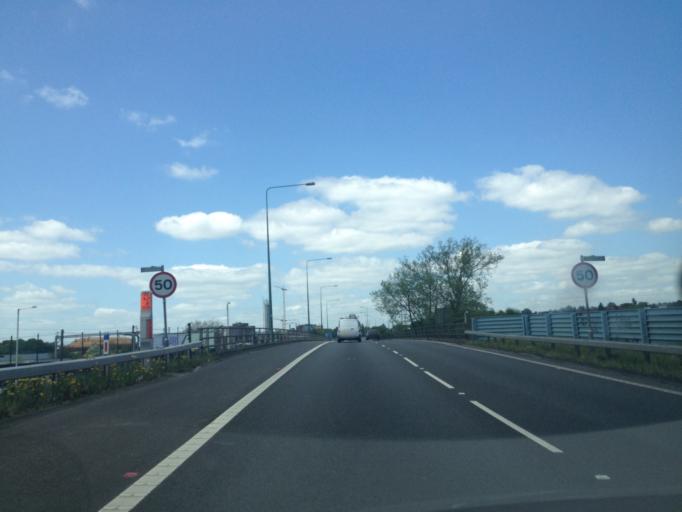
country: GB
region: England
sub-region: Greater London
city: Hendon
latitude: 51.5722
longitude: -0.2292
